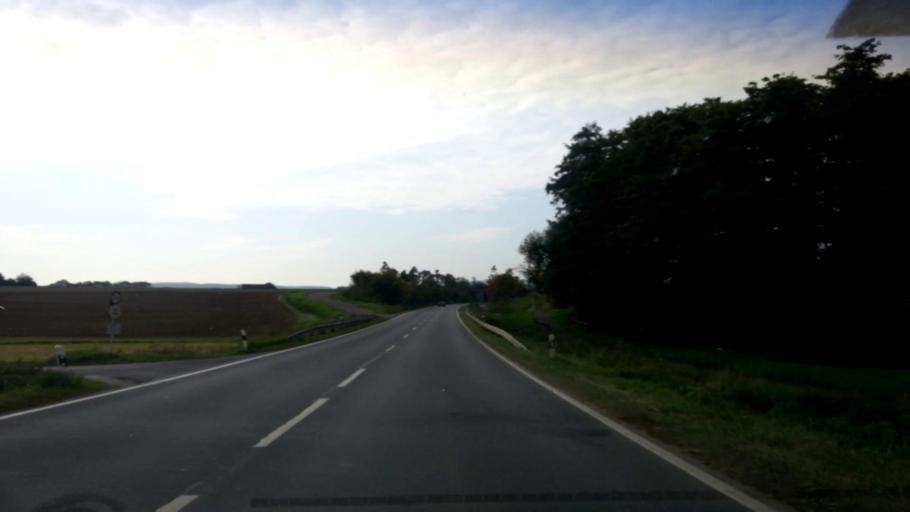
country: DE
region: Bavaria
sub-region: Regierungsbezirk Unterfranken
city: Wiesentheid
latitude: 49.7785
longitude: 10.3424
